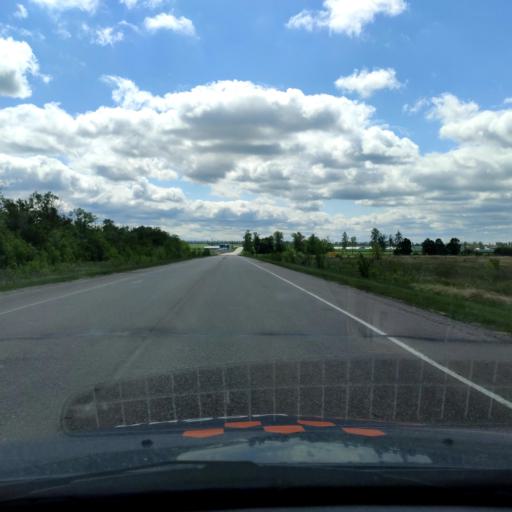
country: RU
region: Voronezj
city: Novaya Usman'
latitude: 51.6110
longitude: 39.3372
